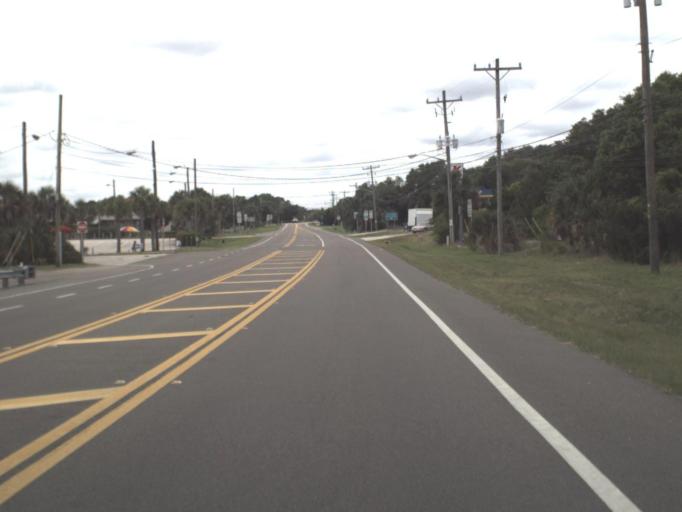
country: US
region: Florida
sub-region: Duval County
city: Atlantic Beach
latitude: 30.3963
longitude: -81.4368
